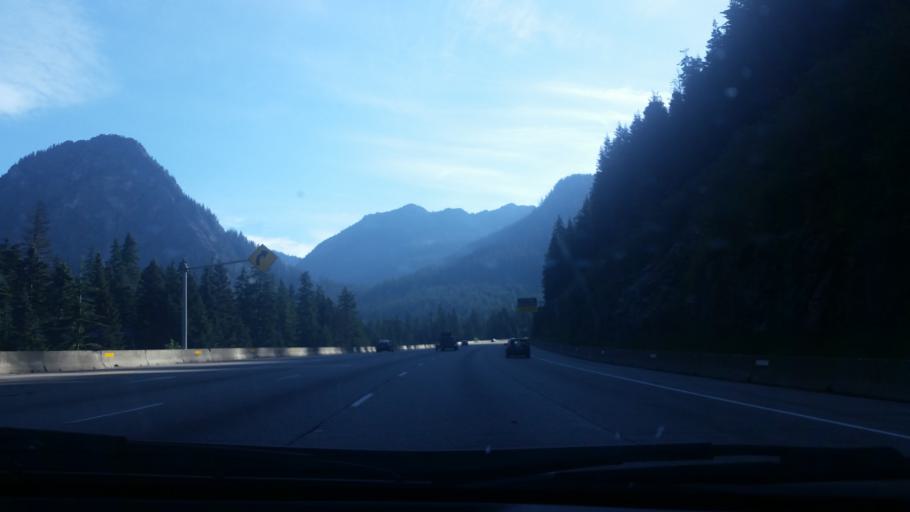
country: US
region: Washington
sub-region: King County
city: Tanner
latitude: 47.4270
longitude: -121.4259
